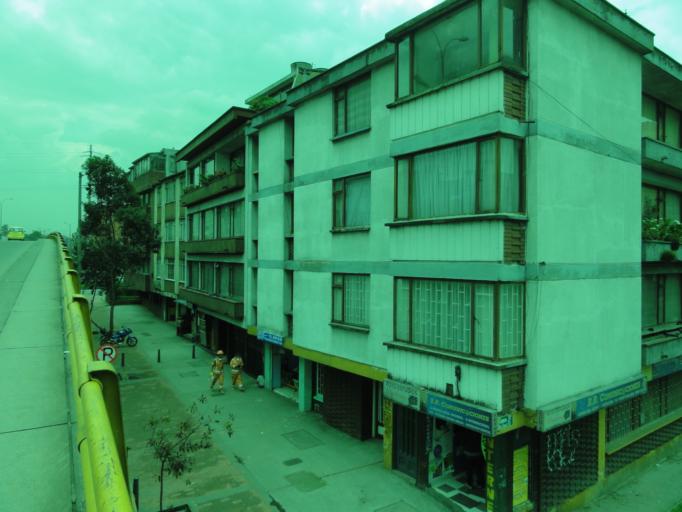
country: CO
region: Bogota D.C.
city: Bogota
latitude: 4.6426
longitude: -74.0785
